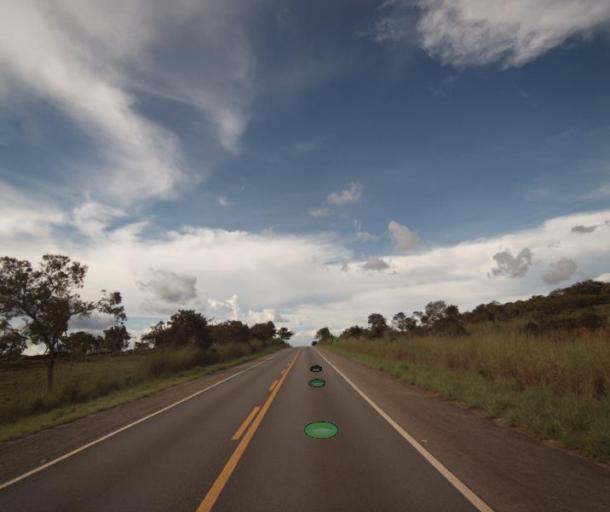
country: BR
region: Goias
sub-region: Barro Alto
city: Barro Alto
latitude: -15.0767
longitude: -48.7293
